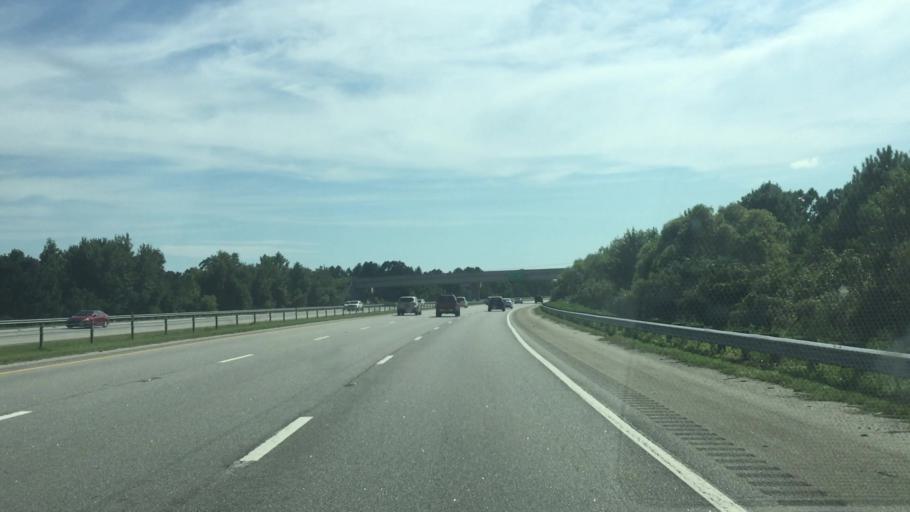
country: US
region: South Carolina
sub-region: Horry County
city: North Myrtle Beach
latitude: 33.8191
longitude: -78.7390
